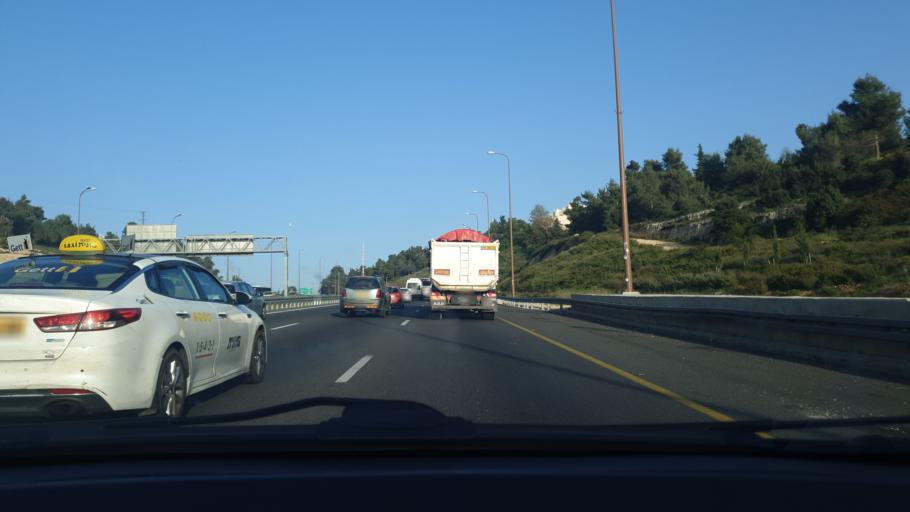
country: PS
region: West Bank
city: Bayt Surik
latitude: 31.7995
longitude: 35.1374
